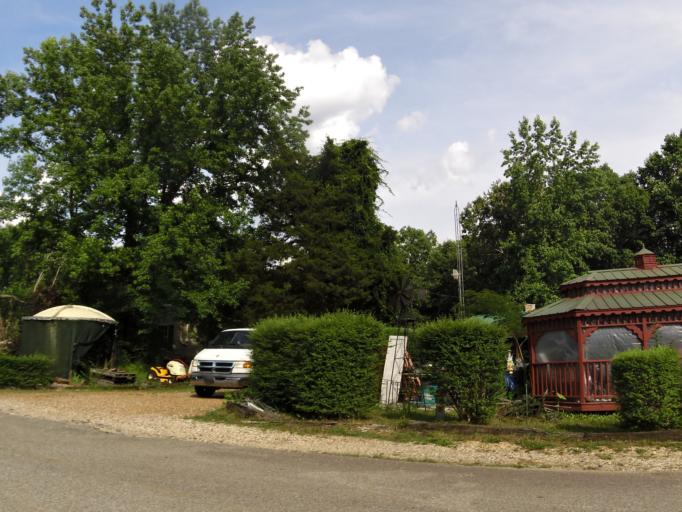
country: US
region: Tennessee
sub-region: Benton County
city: Camden
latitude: 36.0555
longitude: -88.1659
